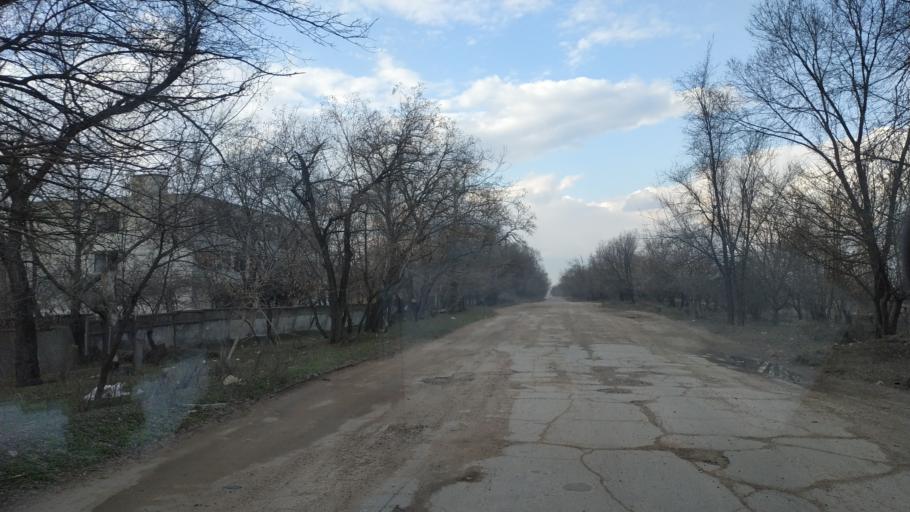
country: MD
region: Anenii Noi
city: Varnita
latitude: 46.8931
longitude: 29.4626
